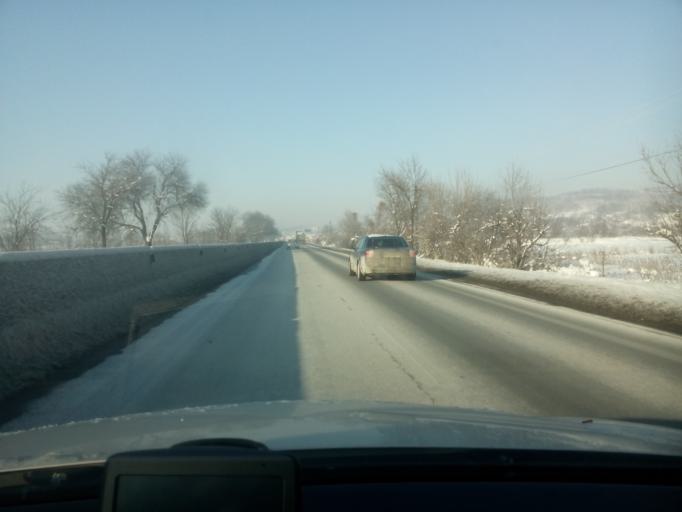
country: RO
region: Sibiu
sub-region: Comuna Selimbar
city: Vestem
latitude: 45.7055
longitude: 24.2461
